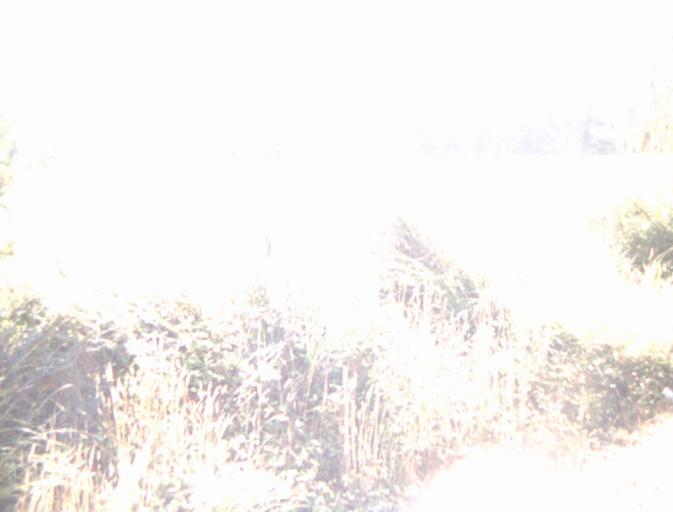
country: AU
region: Tasmania
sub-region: Dorset
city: Bridport
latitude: -41.1557
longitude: 147.2339
